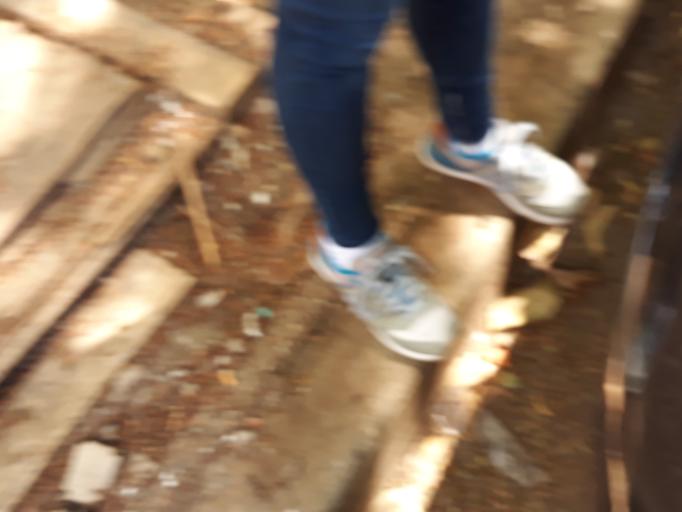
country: CO
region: Valle del Cauca
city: Cali
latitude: 3.3781
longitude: -76.5417
